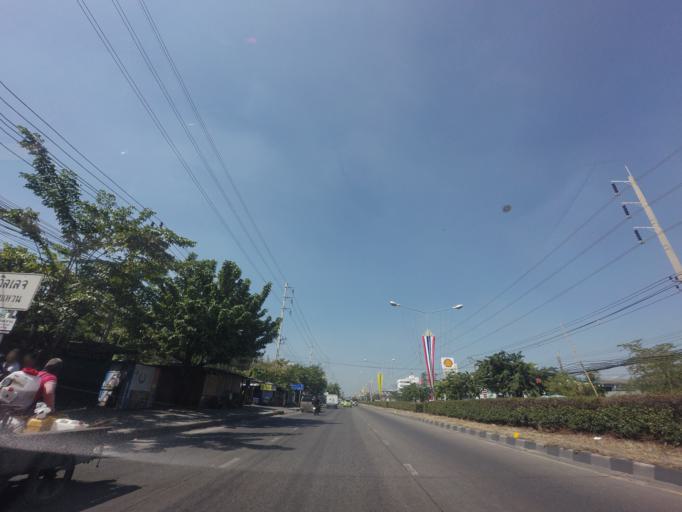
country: TH
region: Bangkok
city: Bang Na
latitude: 13.6095
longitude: 100.6776
